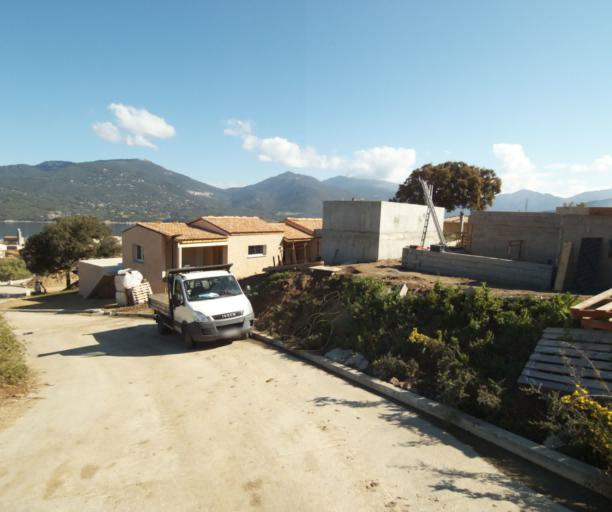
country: FR
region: Corsica
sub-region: Departement de la Corse-du-Sud
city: Propriano
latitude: 41.6684
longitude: 8.9071
